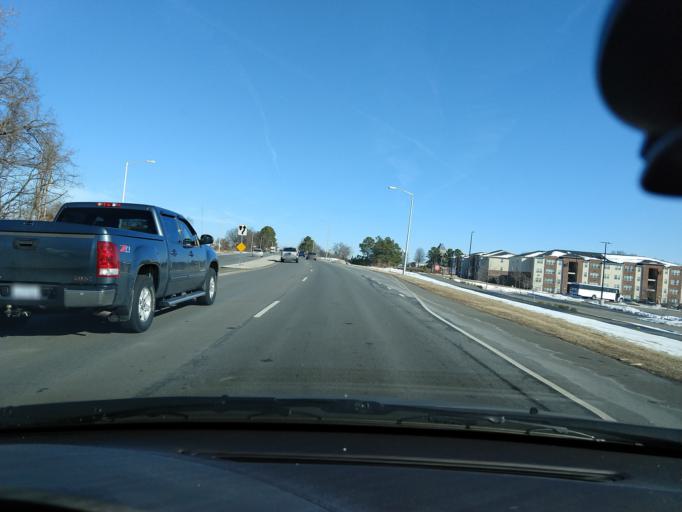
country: US
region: North Carolina
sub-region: Guilford County
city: Greensboro
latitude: 36.0602
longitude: -79.8006
